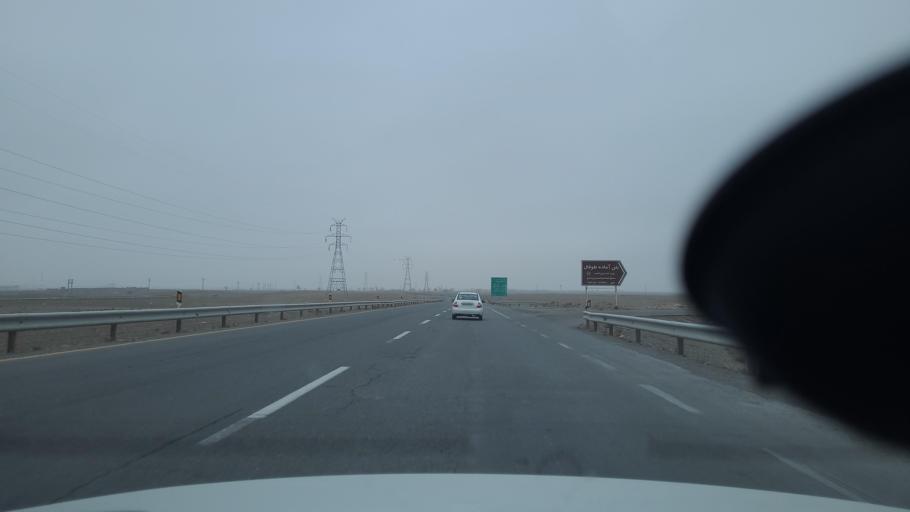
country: IR
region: Razavi Khorasan
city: Fariman
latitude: 35.9721
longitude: 59.7476
